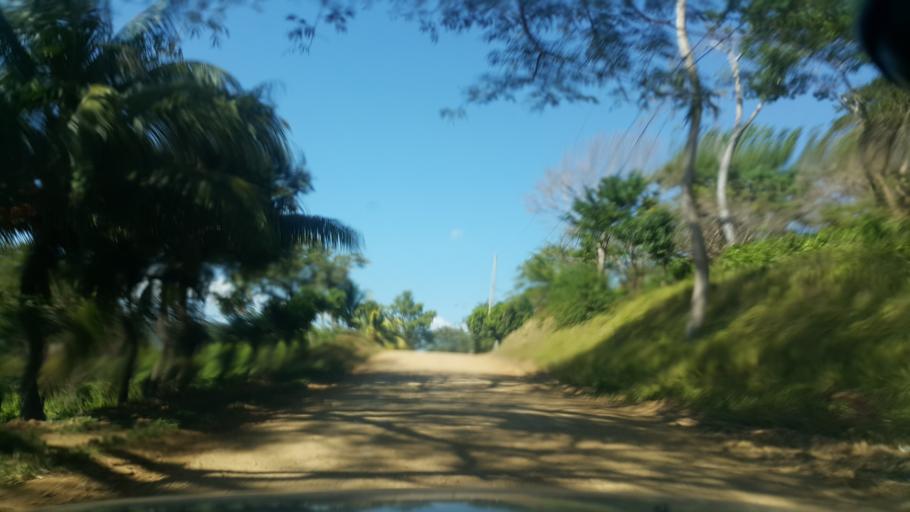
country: NI
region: Rivas
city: San Juan del Sur
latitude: 11.2848
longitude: -85.8771
